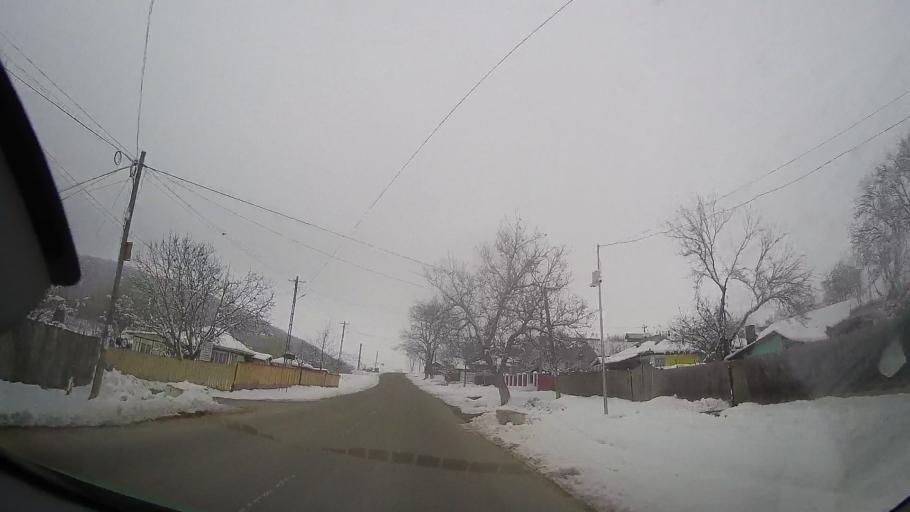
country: RO
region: Neamt
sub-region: Comuna Oniceni
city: Oniceni
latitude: 46.7997
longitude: 27.1439
